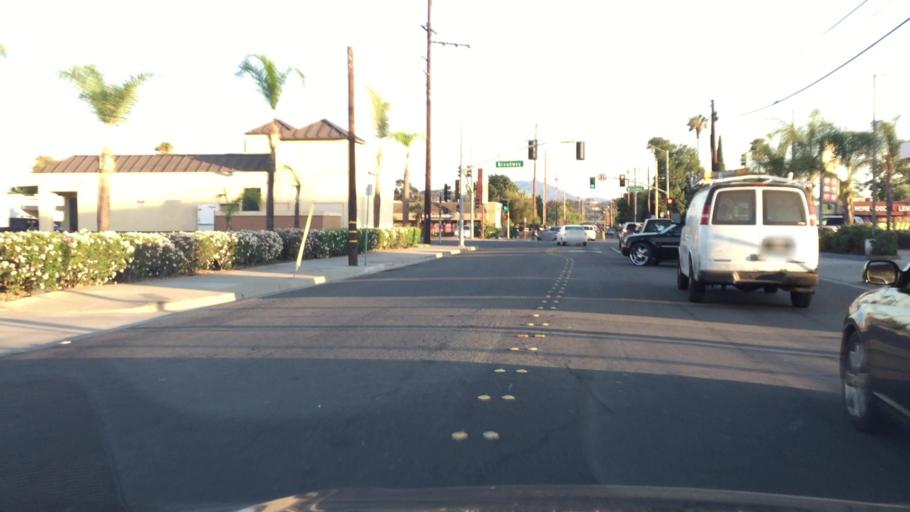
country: US
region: California
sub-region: San Diego County
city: Bostonia
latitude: 32.8084
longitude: -116.9446
